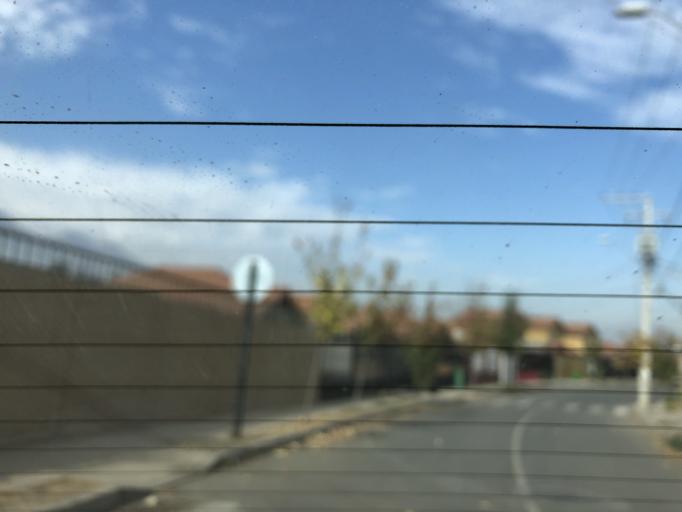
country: CL
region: Santiago Metropolitan
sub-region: Provincia de Cordillera
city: Puente Alto
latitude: -33.5879
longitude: -70.5306
